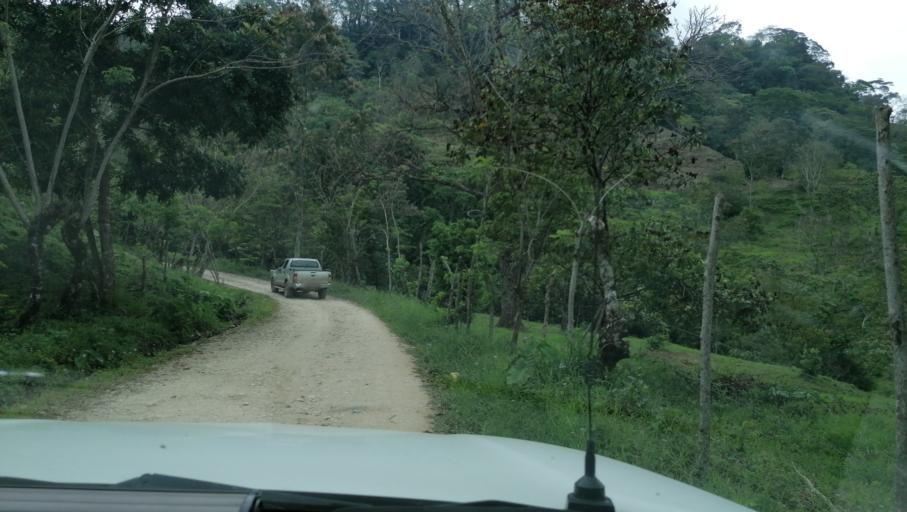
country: MX
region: Chiapas
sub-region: Ocotepec
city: San Pablo Huacano
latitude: 17.2742
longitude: -93.2417
